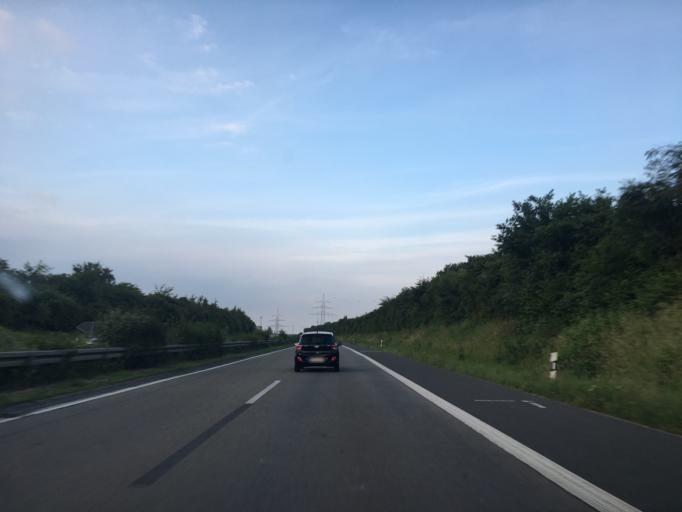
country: DE
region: North Rhine-Westphalia
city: Huckelhoven
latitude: 51.0609
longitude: 6.1950
